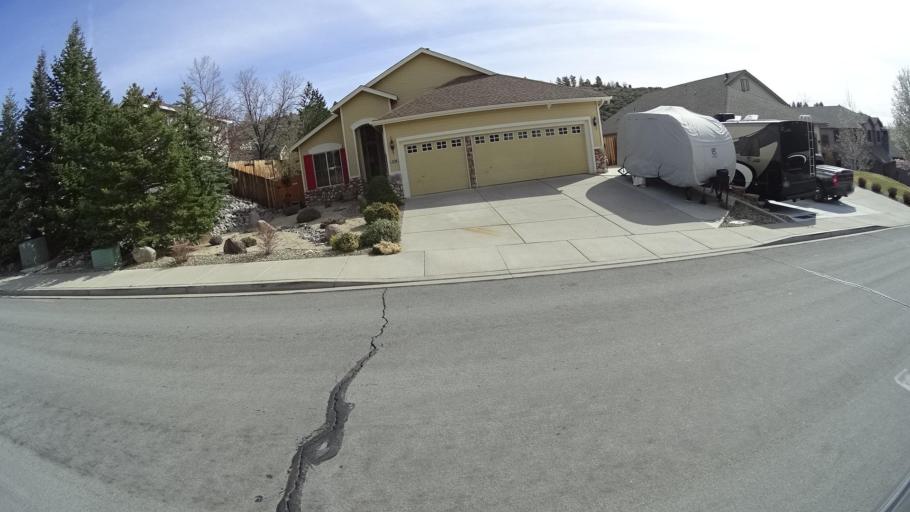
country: US
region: Nevada
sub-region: Washoe County
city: Mogul
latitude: 39.5435
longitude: -119.8966
